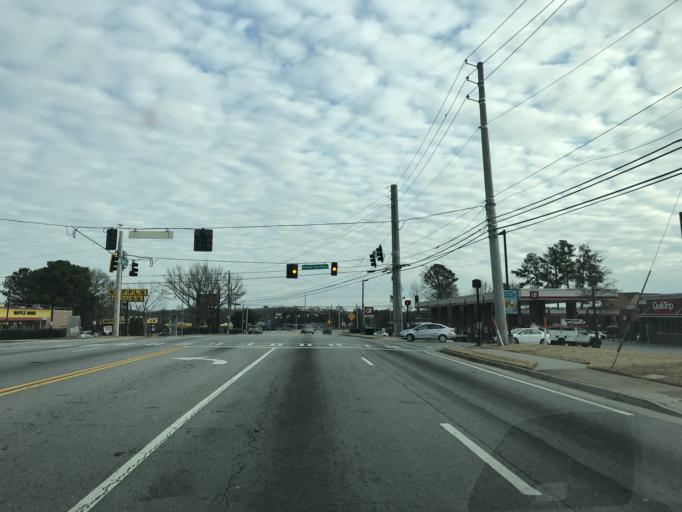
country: US
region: Georgia
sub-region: DeKalb County
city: Doraville
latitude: 33.8805
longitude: -84.2750
